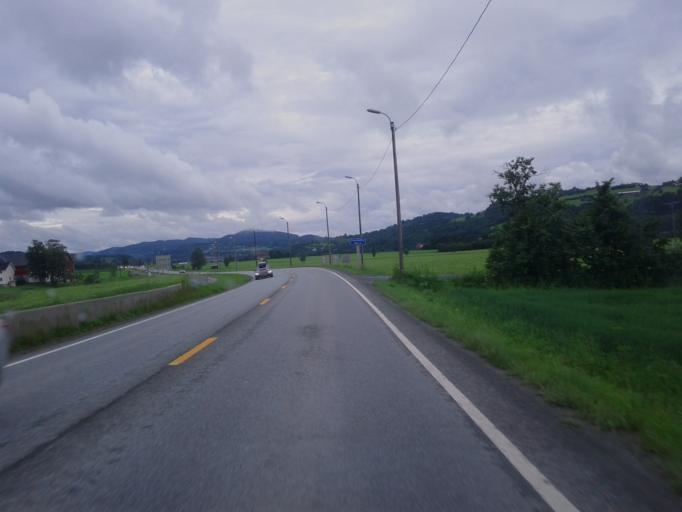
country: NO
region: Sor-Trondelag
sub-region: Melhus
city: Melhus
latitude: 63.3199
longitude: 10.2994
